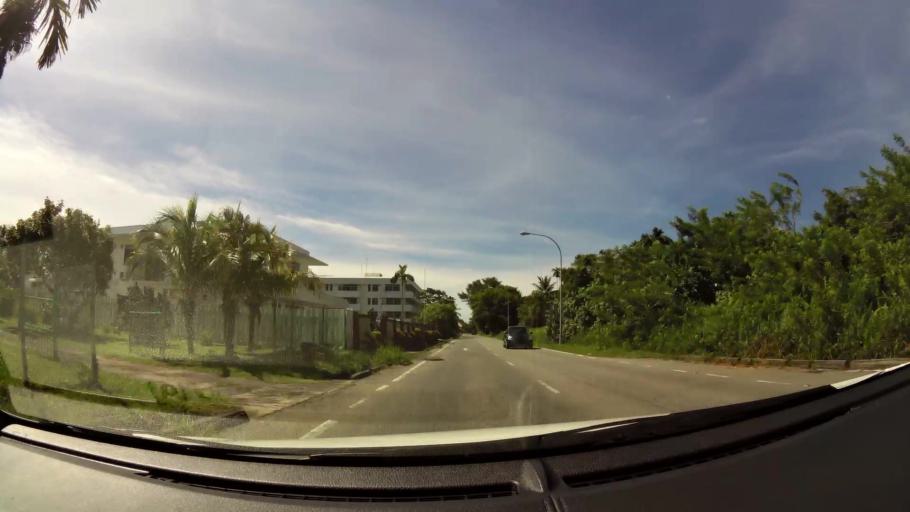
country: BN
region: Belait
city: Kuala Belait
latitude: 4.5883
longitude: 114.2185
